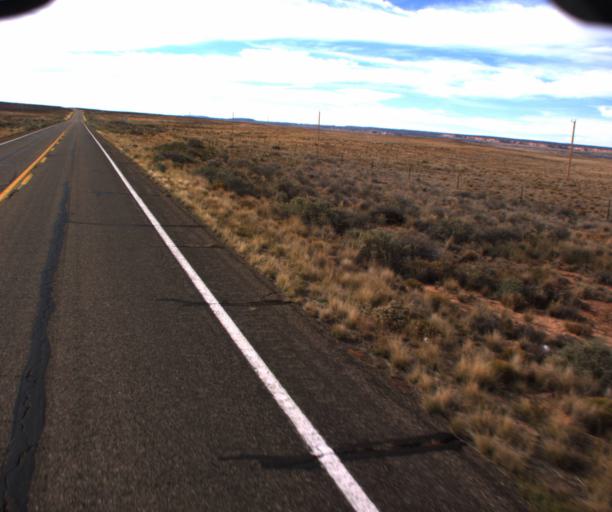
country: US
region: Arizona
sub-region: Coconino County
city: LeChee
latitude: 36.7523
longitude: -111.2849
